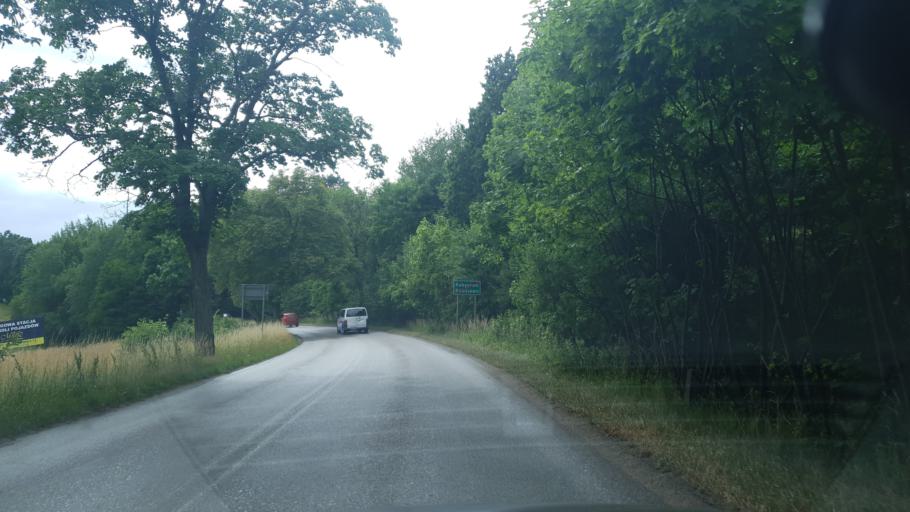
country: PL
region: Pomeranian Voivodeship
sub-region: Powiat kartuski
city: Kartuzy
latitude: 54.3565
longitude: 18.2360
